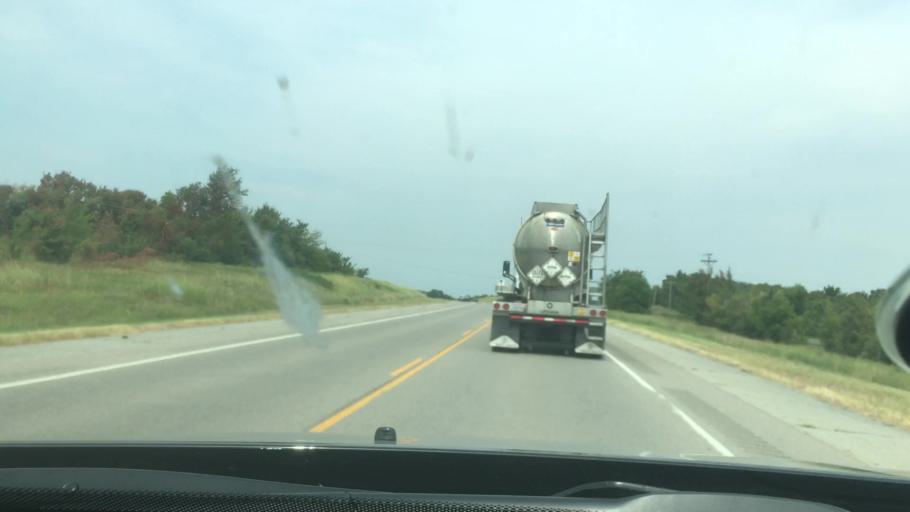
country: US
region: Oklahoma
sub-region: Pontotoc County
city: Ada
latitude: 34.6419
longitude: -96.4909
